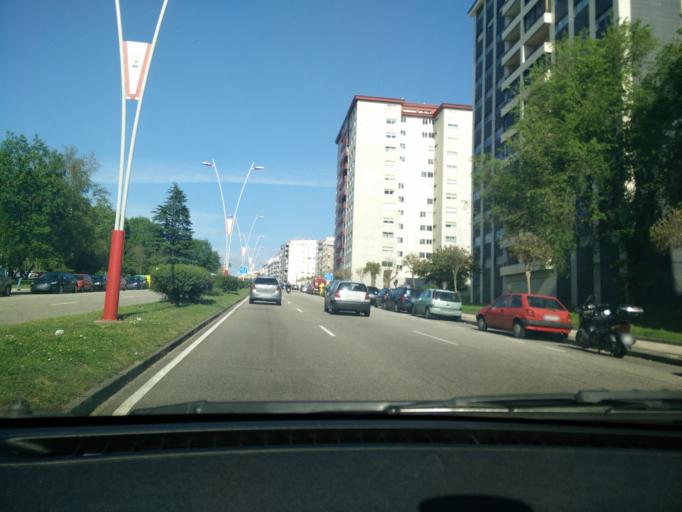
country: ES
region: Galicia
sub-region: Provincia de Pontevedra
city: Vigo
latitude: 42.2179
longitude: -8.7471
